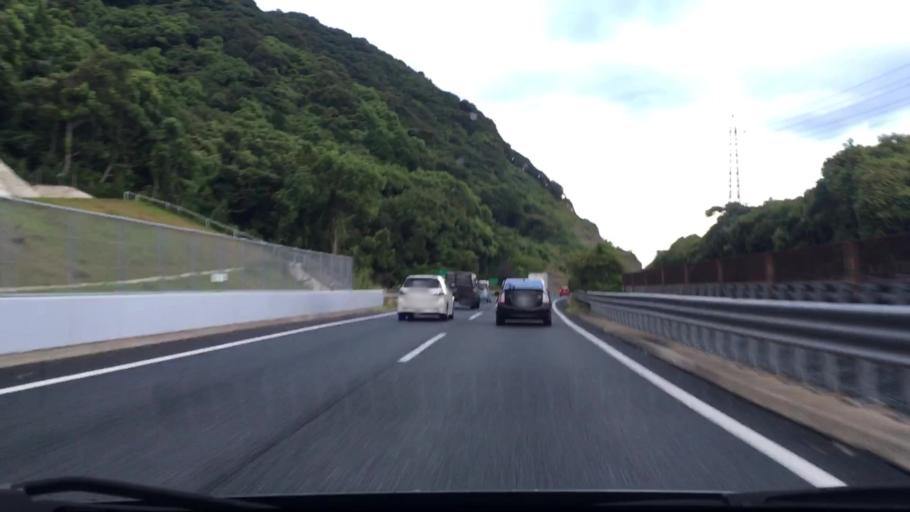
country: JP
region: Yamaguchi
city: Shimonoseki
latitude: 33.8643
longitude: 130.9455
